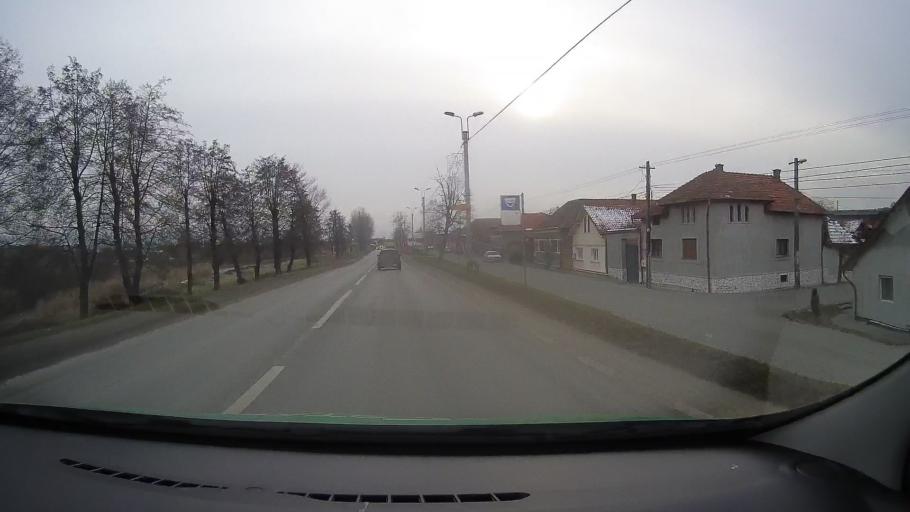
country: RO
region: Hunedoara
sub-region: Municipiul Orastie
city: Orastie
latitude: 45.8533
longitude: 23.2079
